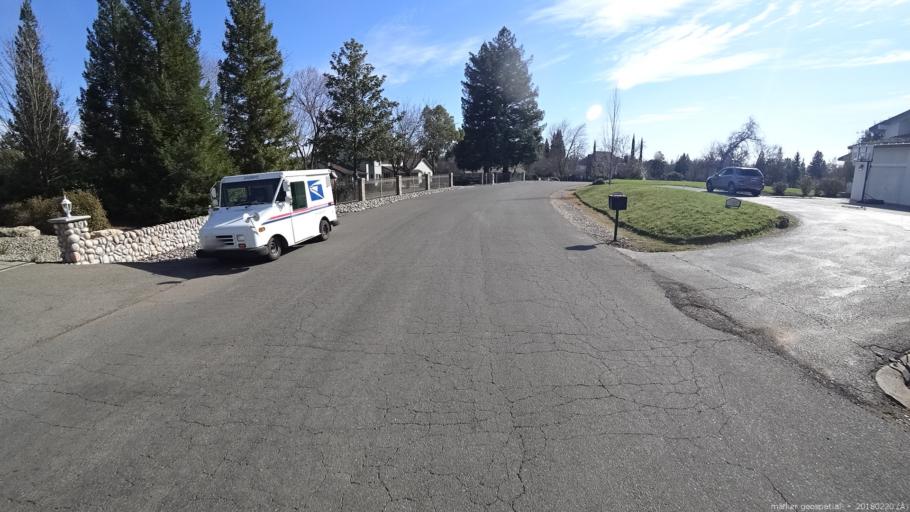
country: US
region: California
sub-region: Sacramento County
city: Orangevale
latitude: 38.7110
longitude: -121.2314
